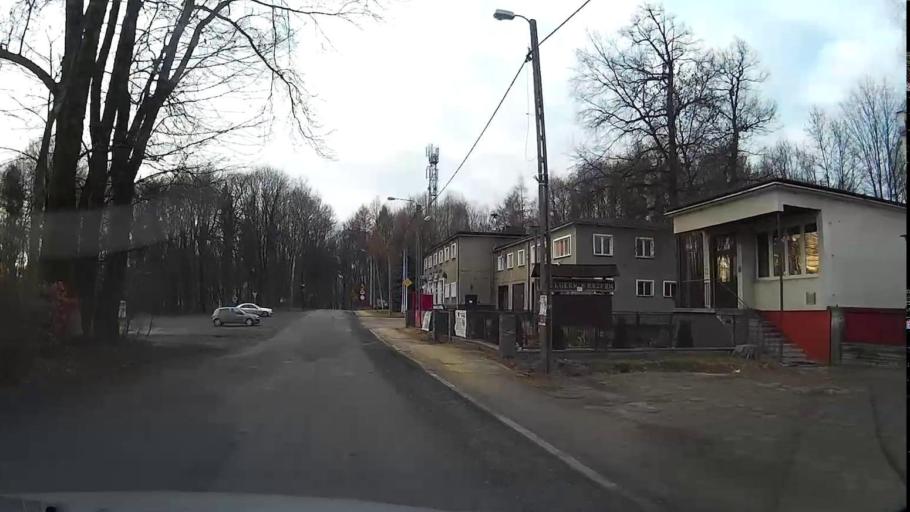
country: PL
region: Lesser Poland Voivodeship
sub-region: Powiat chrzanowski
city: Alwernia
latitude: 50.0691
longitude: 19.5370
